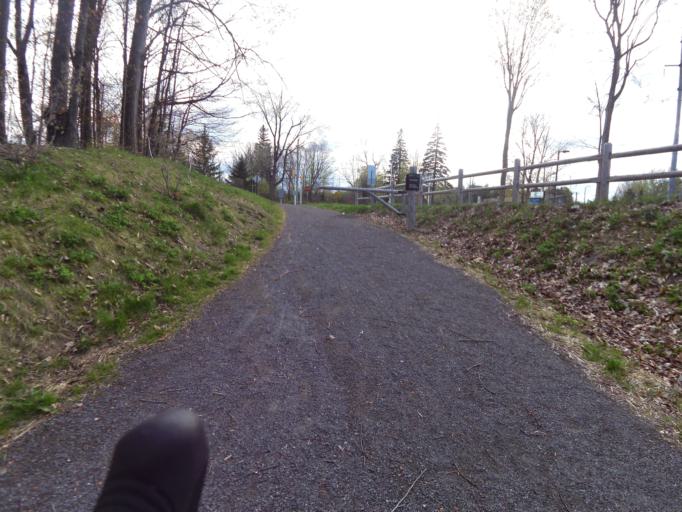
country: CA
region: Ontario
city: Ottawa
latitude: 45.3175
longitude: -75.7133
